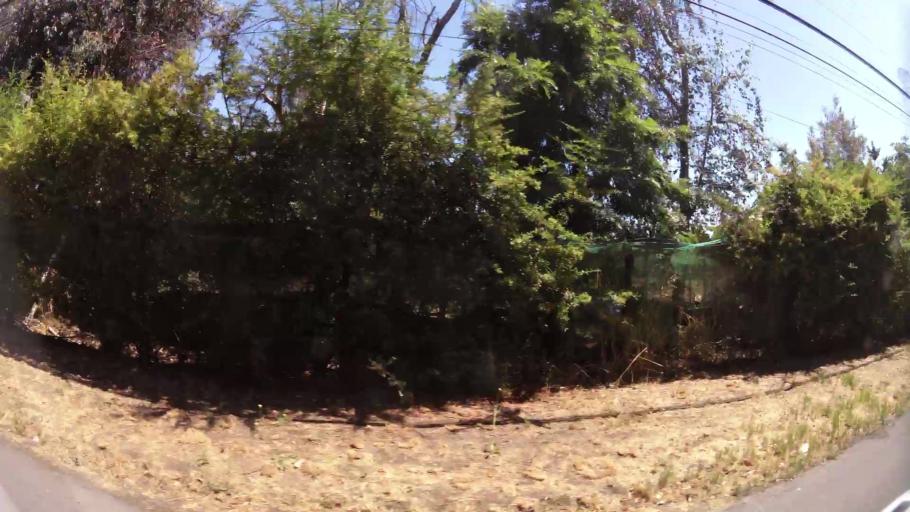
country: CL
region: Maule
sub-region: Provincia de Curico
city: Curico
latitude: -34.9932
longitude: -71.2113
